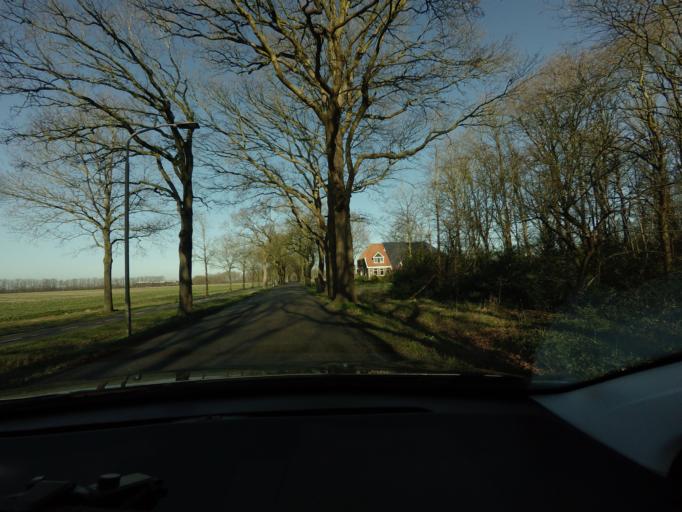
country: NL
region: Drenthe
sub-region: Gemeente Assen
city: Assen
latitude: 52.8575
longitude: 6.5932
